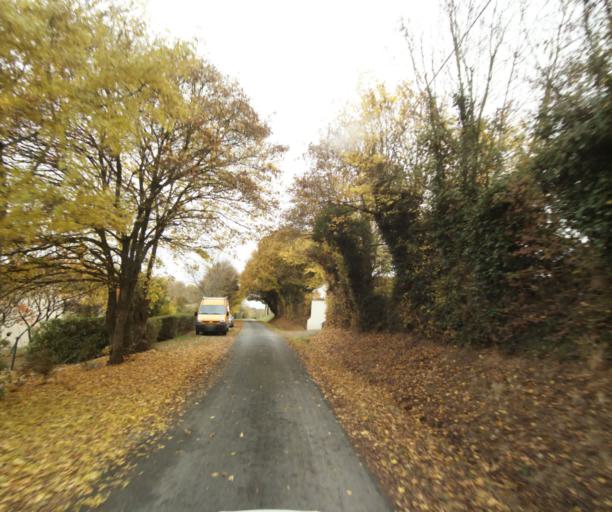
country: FR
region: Poitou-Charentes
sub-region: Departement de la Charente-Maritime
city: Bussac-sur-Charente
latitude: 45.7708
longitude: -0.6455
